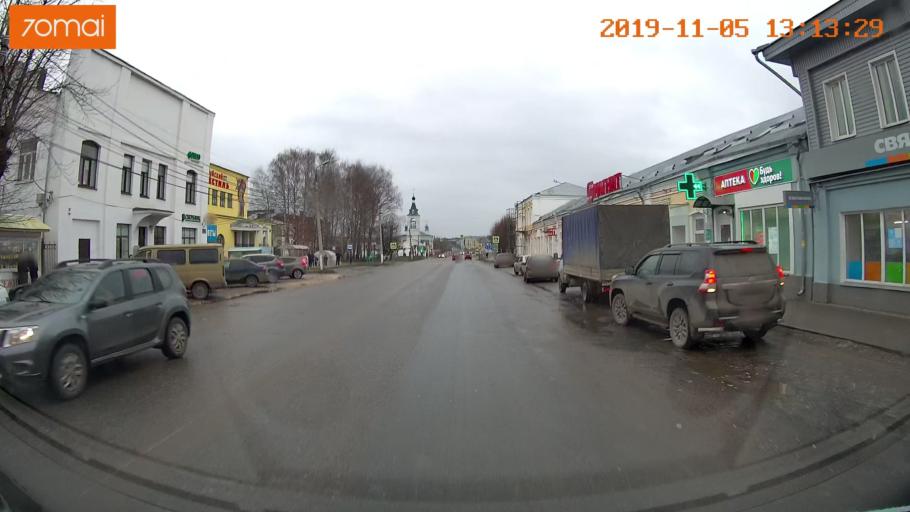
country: RU
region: Ivanovo
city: Shuya
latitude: 56.8512
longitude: 41.3549
